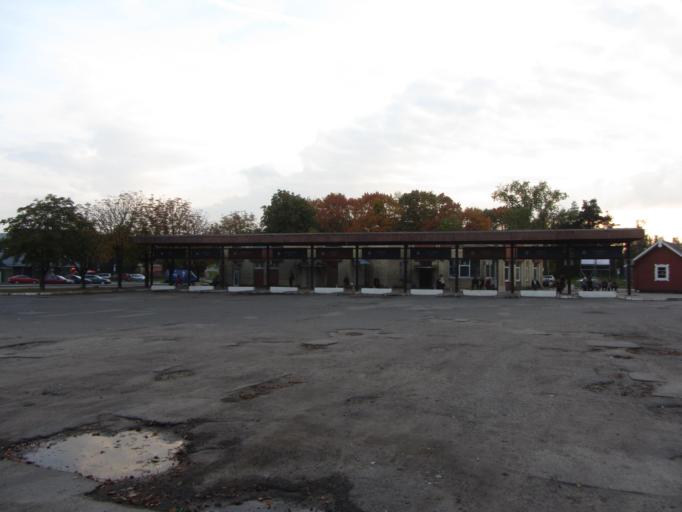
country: LT
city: Trakai
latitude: 54.6338
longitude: 24.9353
